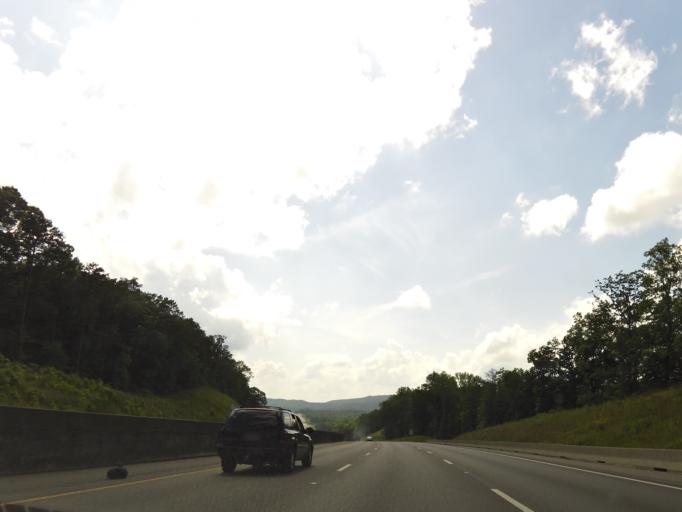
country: US
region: Alabama
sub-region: Saint Clair County
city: Odenville
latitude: 33.5963
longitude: -86.3739
